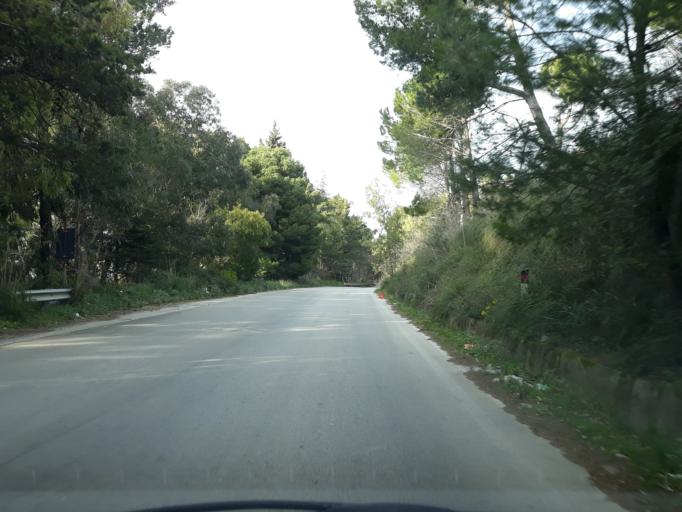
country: IT
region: Sicily
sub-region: Palermo
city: Torretta
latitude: 38.1103
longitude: 13.2382
